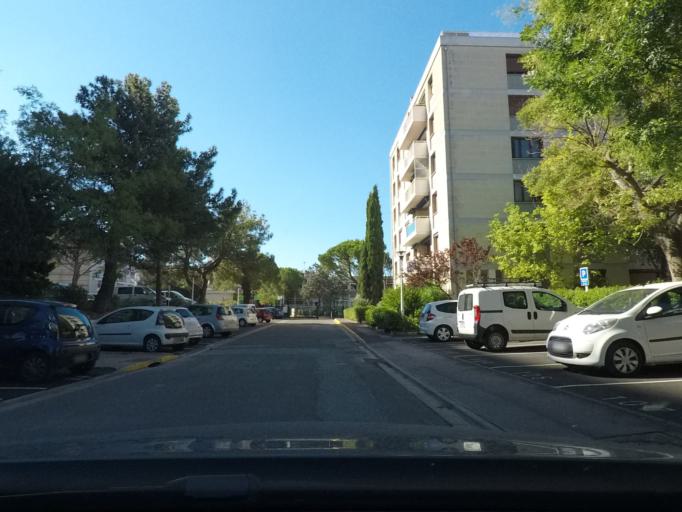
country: FR
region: Provence-Alpes-Cote d'Azur
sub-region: Departement des Bouches-du-Rhone
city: Marseille 09
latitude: 43.2544
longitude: 5.4158
